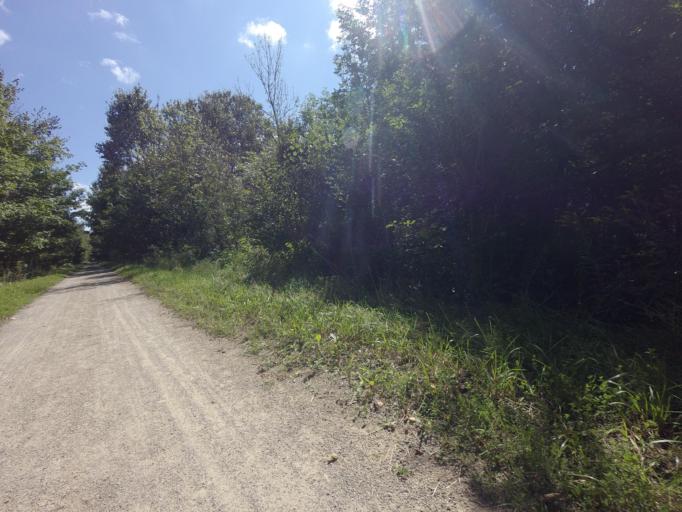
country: CA
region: Ontario
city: Orangeville
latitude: 43.7935
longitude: -80.3050
